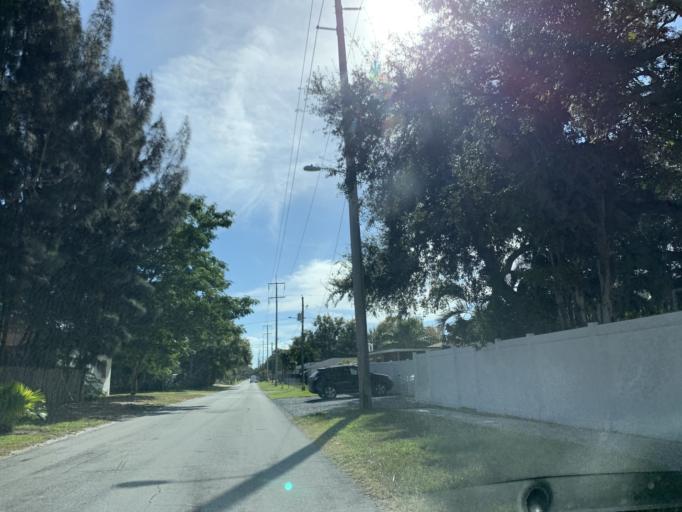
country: US
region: Florida
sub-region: Hillsborough County
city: Tampa
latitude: 27.8889
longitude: -82.4981
